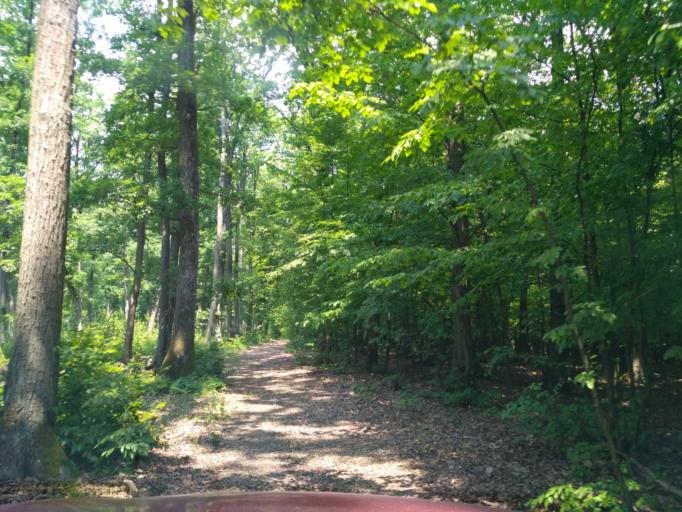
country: SK
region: Kosicky
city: Moldava nad Bodvou
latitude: 48.6429
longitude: 21.0389
